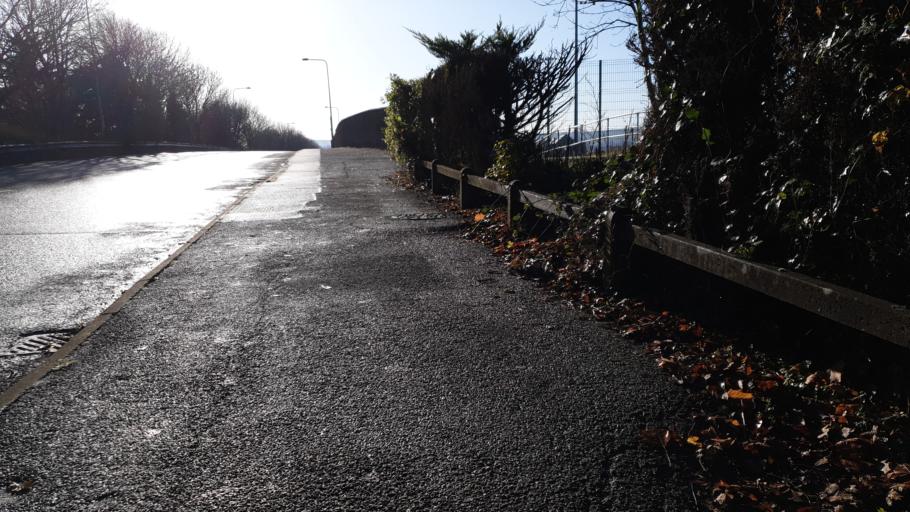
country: IE
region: Munster
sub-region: County Cork
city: Cork
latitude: 51.8912
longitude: -8.4336
